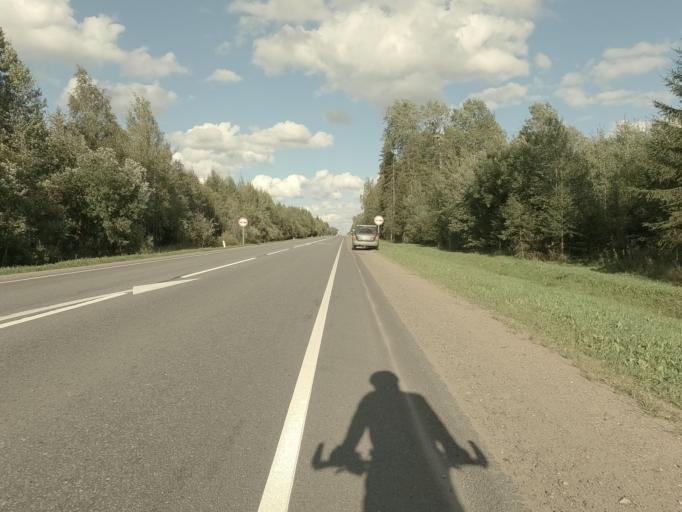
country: RU
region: Leningrad
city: Nikol'skoye
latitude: 59.6685
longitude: 30.8919
